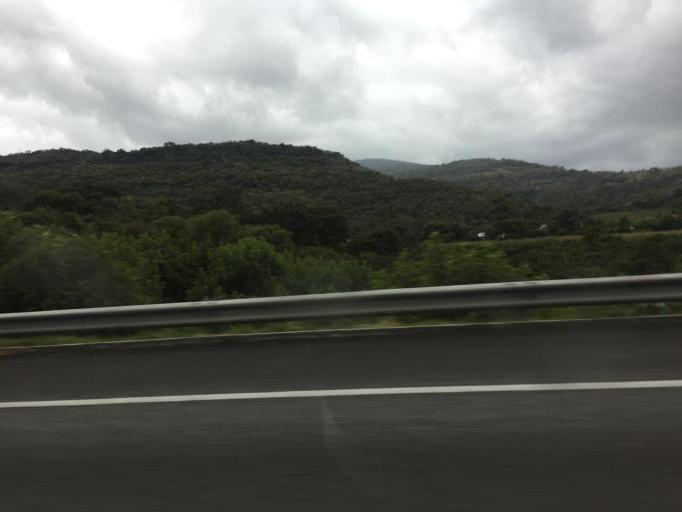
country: MX
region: Jalisco
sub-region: Zapotlanejo
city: La Mezquitera
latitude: 20.5353
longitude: -103.0166
